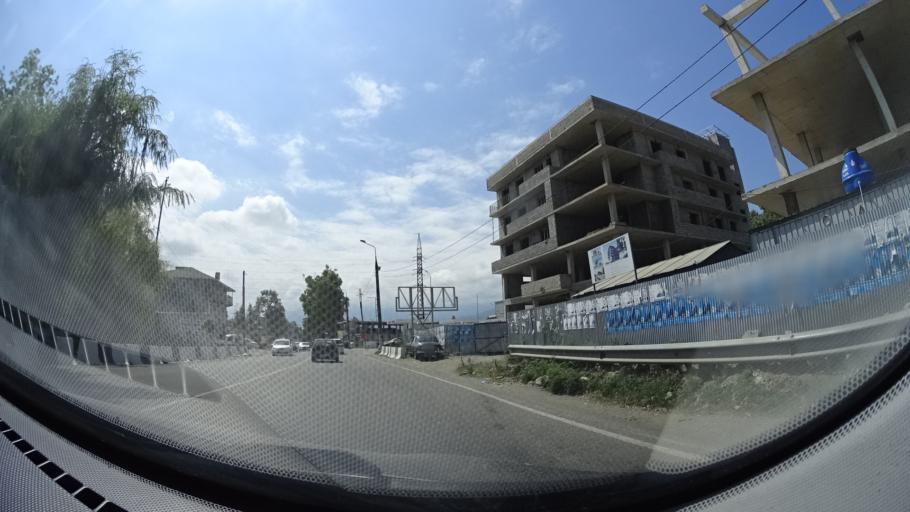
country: GE
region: Ajaria
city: Batumi
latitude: 41.6202
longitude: 41.6169
